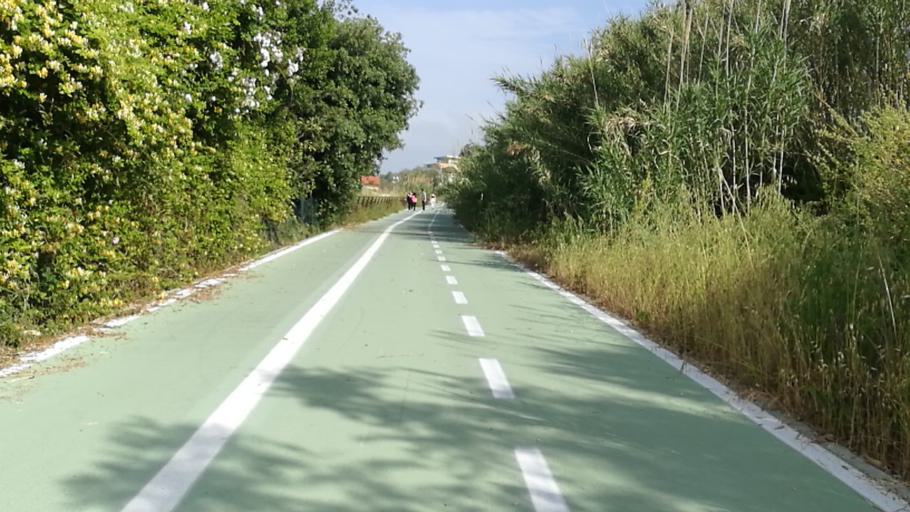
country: IT
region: Abruzzo
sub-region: Provincia di Chieti
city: Torino di Sangro
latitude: 42.2098
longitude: 14.5928
